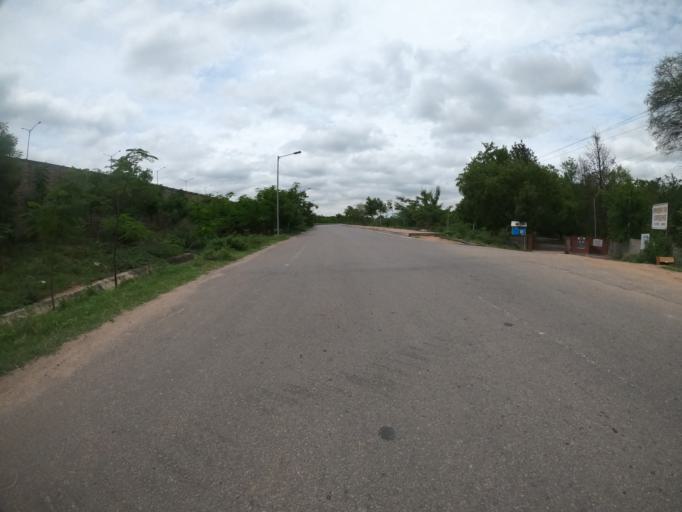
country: IN
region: Telangana
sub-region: Rangareddi
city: Sriramnagar
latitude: 17.2547
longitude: 78.3756
